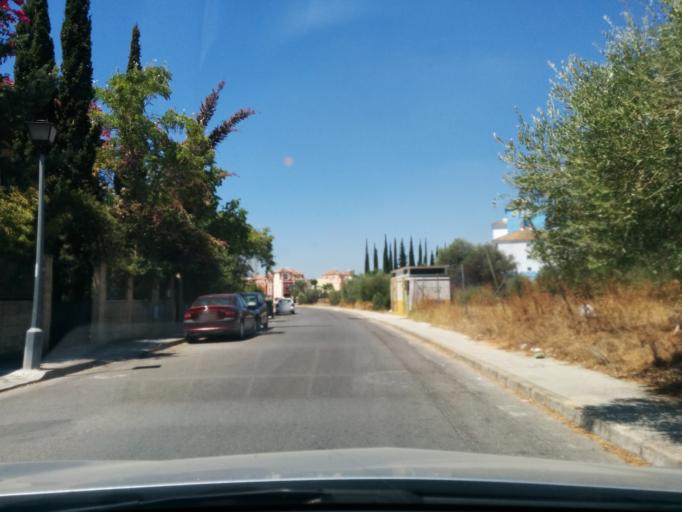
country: ES
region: Andalusia
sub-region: Provincia de Sevilla
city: Benacazon
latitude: 37.3590
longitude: -6.1966
